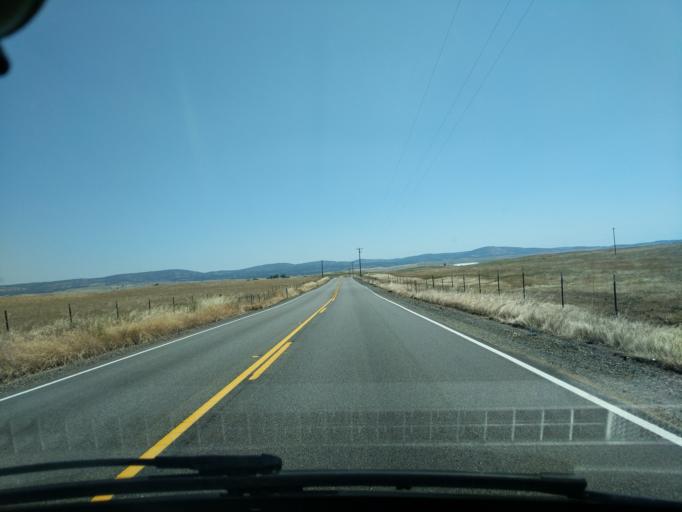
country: US
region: California
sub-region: Stanislaus County
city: East Oakdale
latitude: 37.9446
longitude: -120.8339
